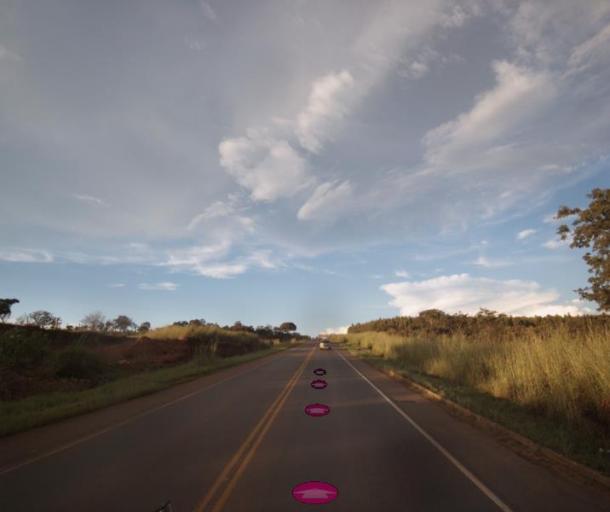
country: BR
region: Goias
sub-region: Anapolis
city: Anapolis
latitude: -16.2292
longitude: -48.9286
